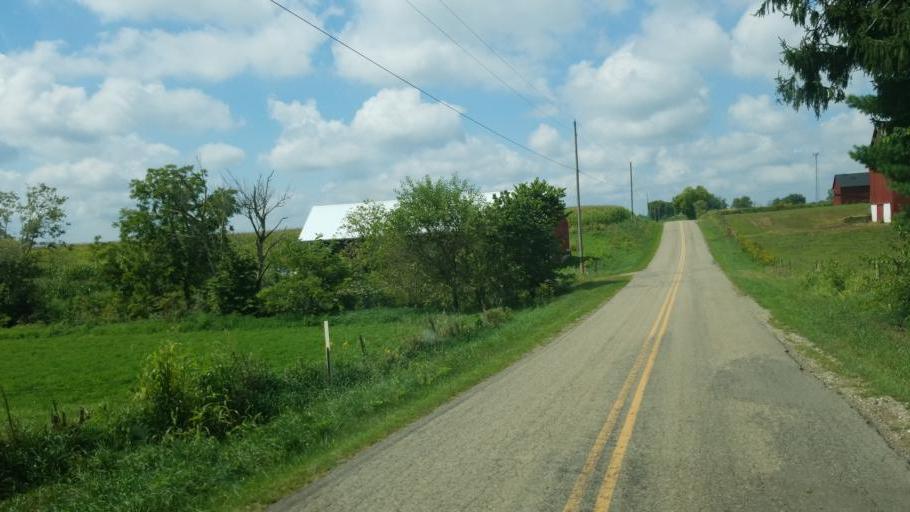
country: US
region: Ohio
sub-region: Licking County
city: Utica
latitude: 40.2667
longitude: -82.4777
